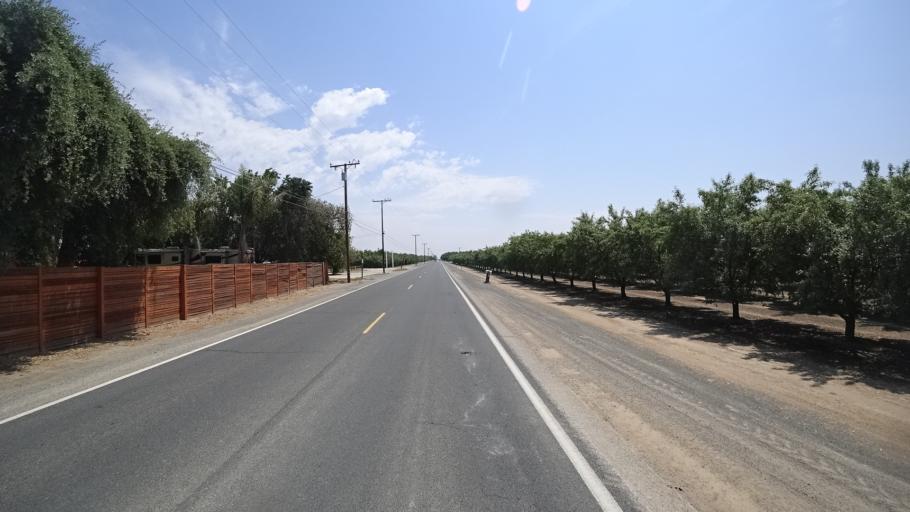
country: US
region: California
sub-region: Kings County
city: Armona
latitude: 36.3281
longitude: -119.7214
